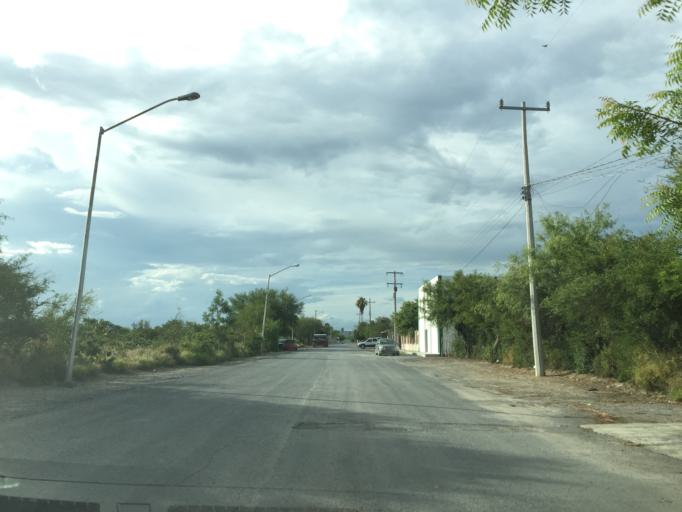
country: MX
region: Nuevo Leon
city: Marin
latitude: 25.8705
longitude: -100.0274
